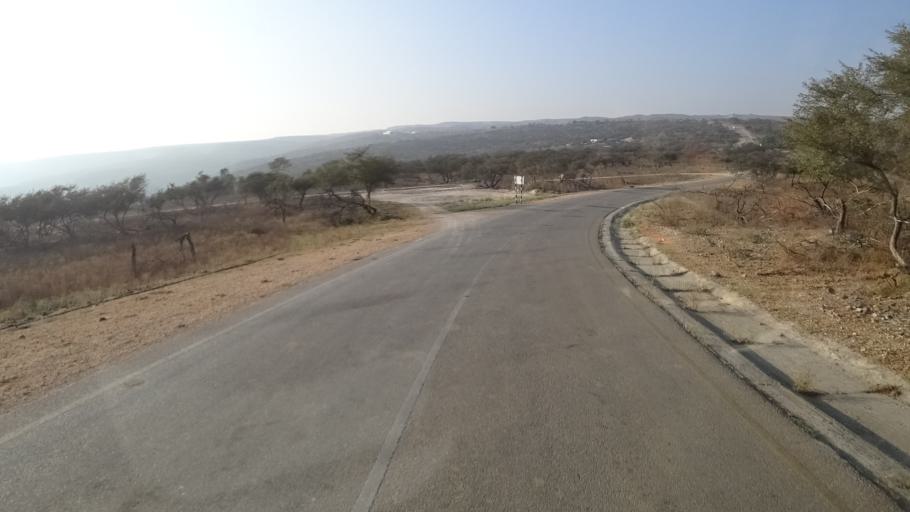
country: YE
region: Al Mahrah
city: Hawf
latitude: 16.7807
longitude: 53.3314
